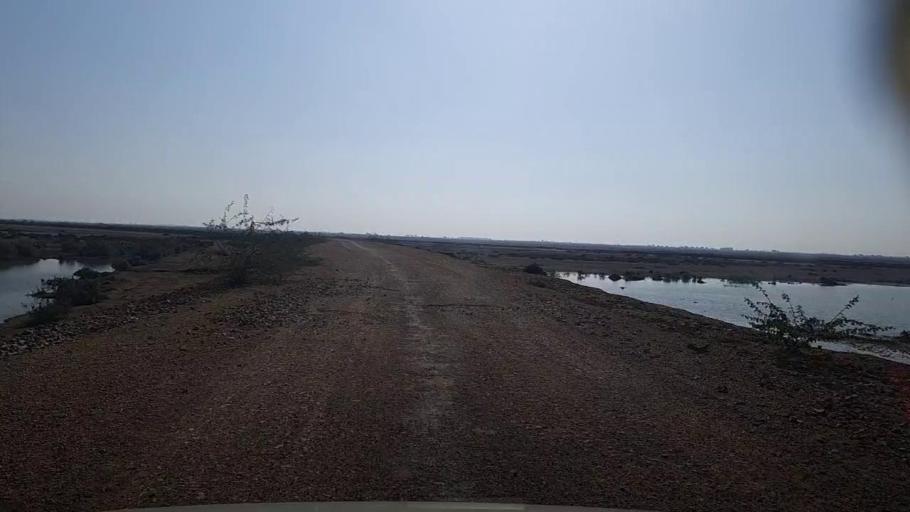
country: PK
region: Sindh
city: Mirpur Sakro
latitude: 24.5177
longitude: 67.4928
